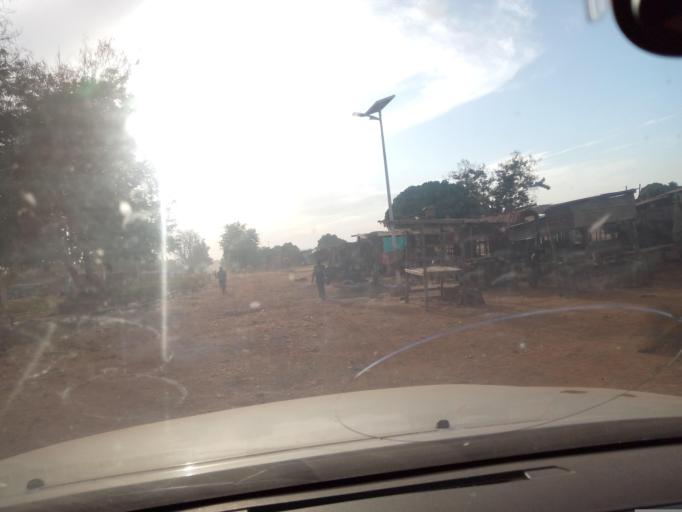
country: ML
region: Sikasso
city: Sikasso
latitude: 11.3145
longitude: -5.6466
